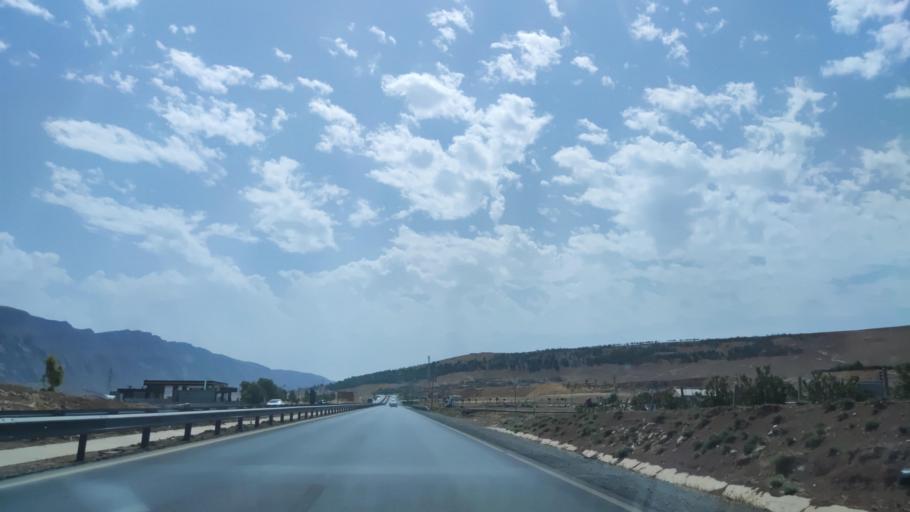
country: IQ
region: Arbil
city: Shaqlawah
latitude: 36.5002
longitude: 44.3590
